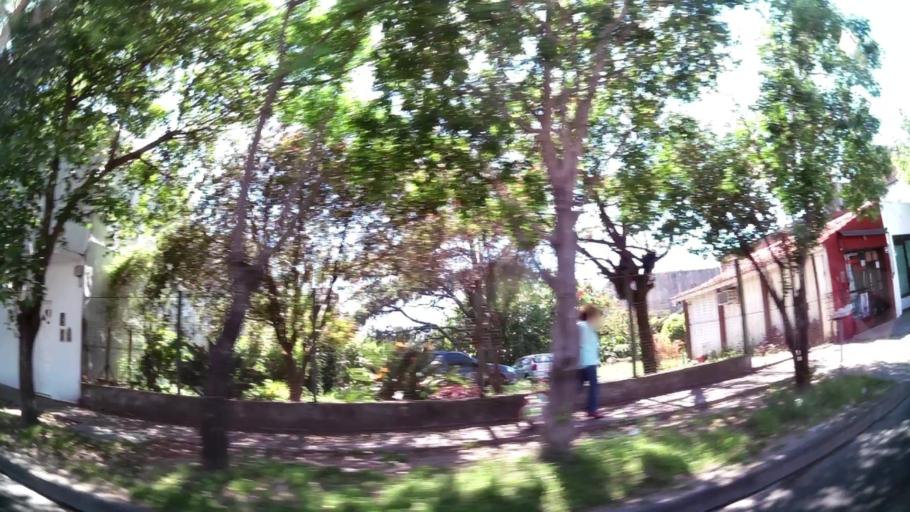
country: AR
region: Buenos Aires
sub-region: Partido de Tigre
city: Tigre
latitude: -34.4880
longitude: -58.6139
